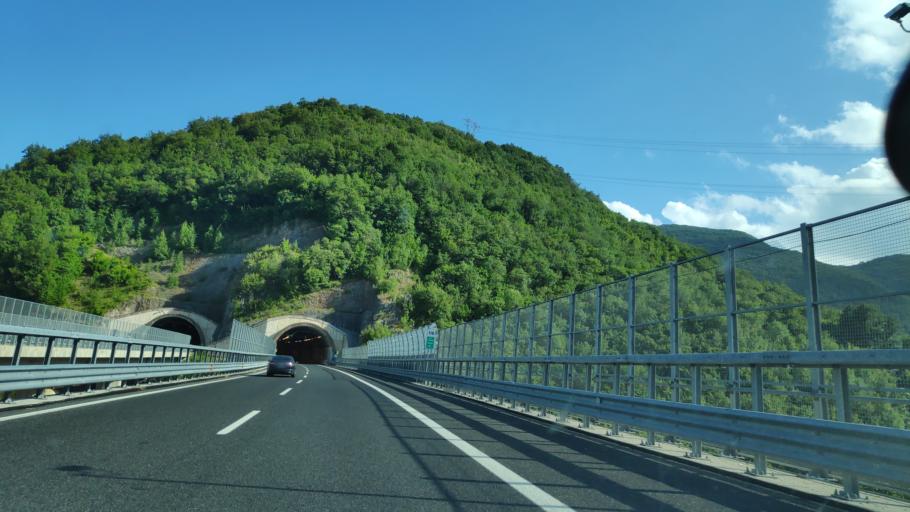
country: IT
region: Campania
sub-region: Provincia di Salerno
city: Casalbuono
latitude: 40.2148
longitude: 15.6724
